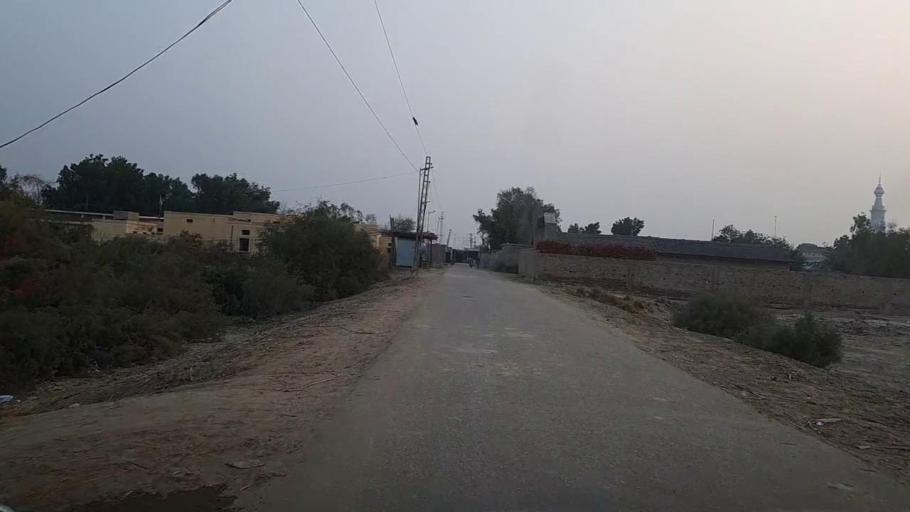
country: PK
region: Sindh
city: Kandiari
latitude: 26.9272
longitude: 68.5008
